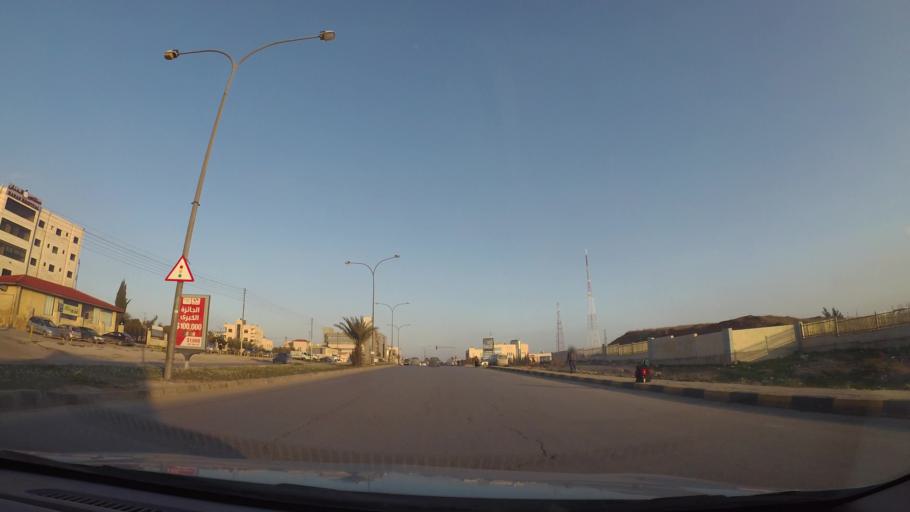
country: JO
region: Amman
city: Al Quwaysimah
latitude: 31.9088
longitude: 35.9282
